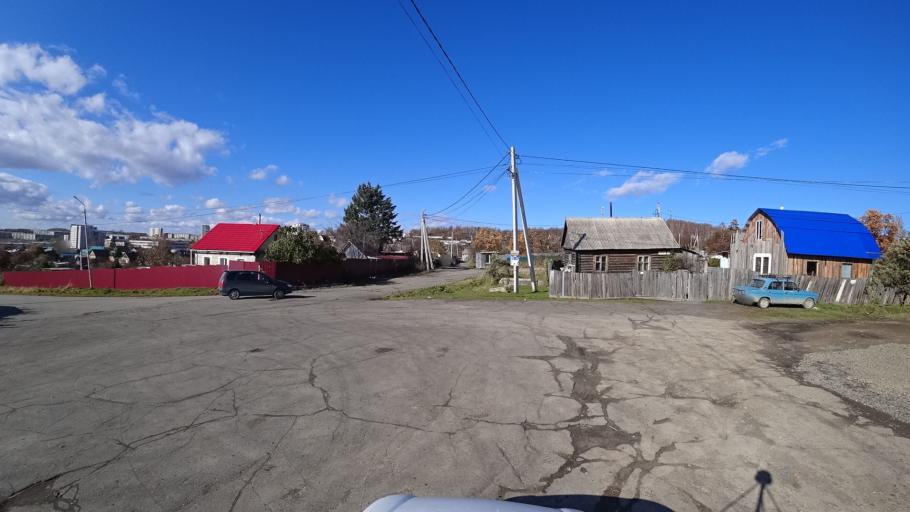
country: RU
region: Khabarovsk Krai
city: Amursk
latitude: 50.2353
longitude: 136.9228
